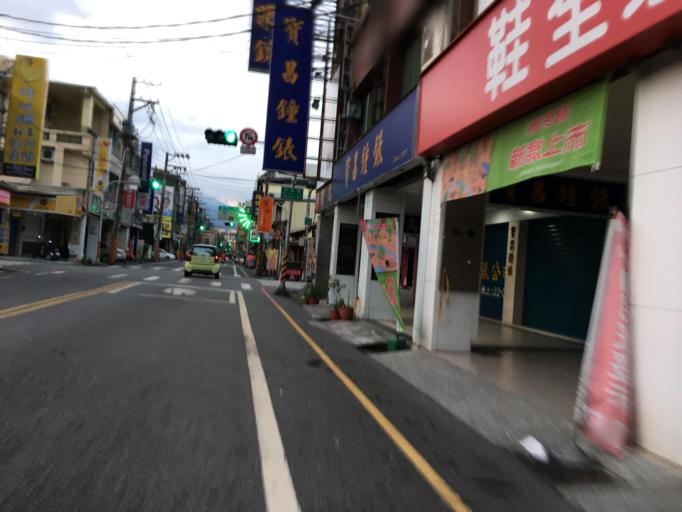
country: TW
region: Taiwan
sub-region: Yilan
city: Yilan
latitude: 24.6754
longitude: 121.7712
